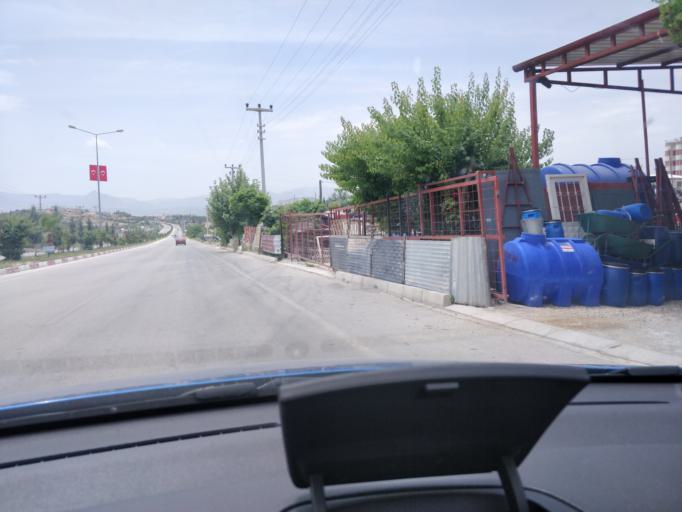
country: TR
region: Mersin
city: Mut
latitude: 36.6280
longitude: 33.4462
